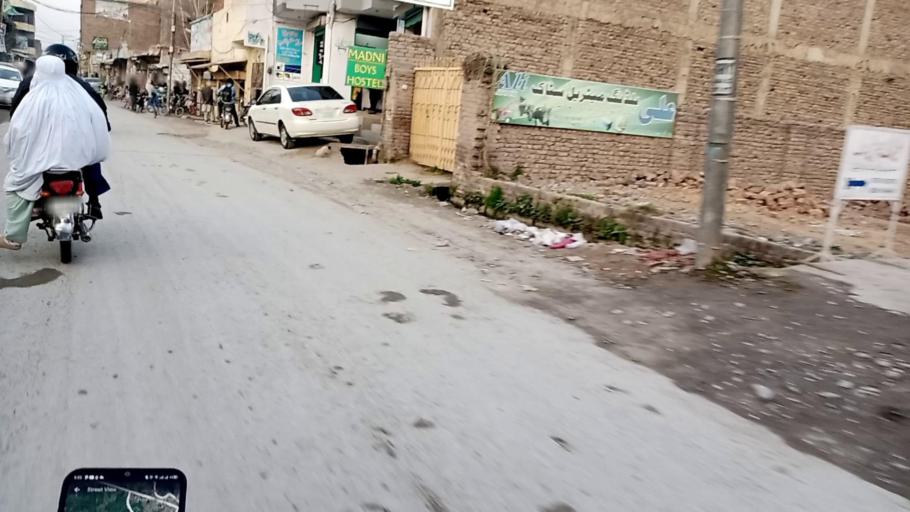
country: PK
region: Khyber Pakhtunkhwa
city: Peshawar
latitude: 34.0254
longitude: 71.4870
